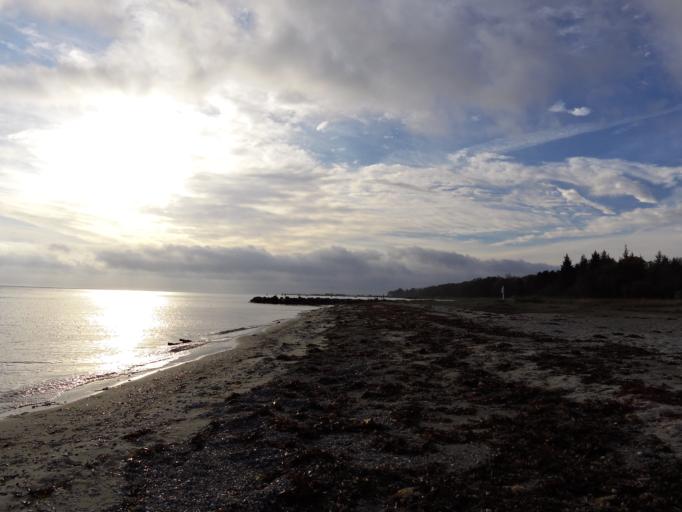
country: DK
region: Central Jutland
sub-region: Odder Kommune
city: Odder
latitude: 55.9259
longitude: 10.2578
